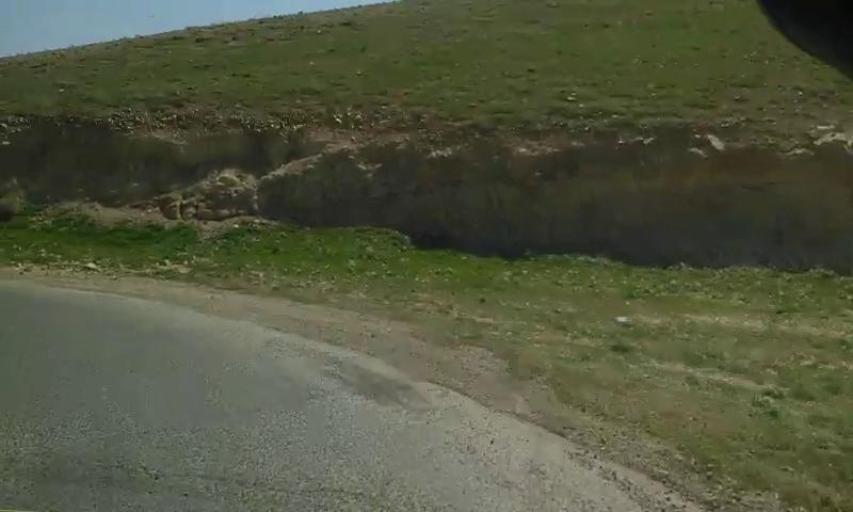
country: PS
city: `Arab ar Rashaydah
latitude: 31.5558
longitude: 35.2477
